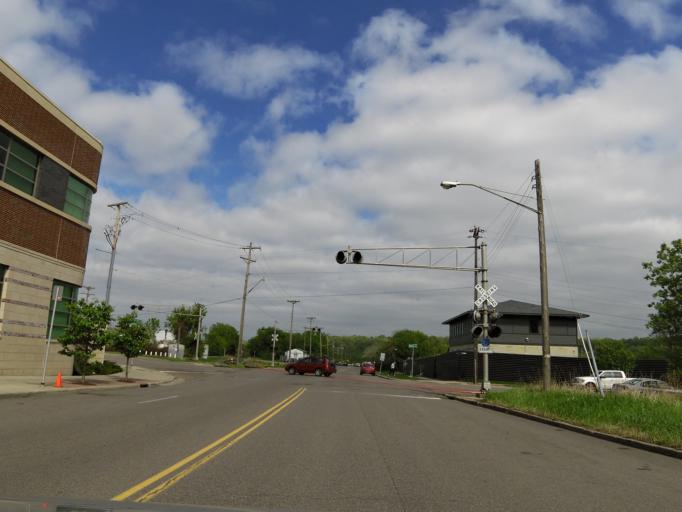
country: US
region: Minnesota
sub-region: Dakota County
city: West Saint Paul
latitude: 44.9269
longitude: -93.1268
